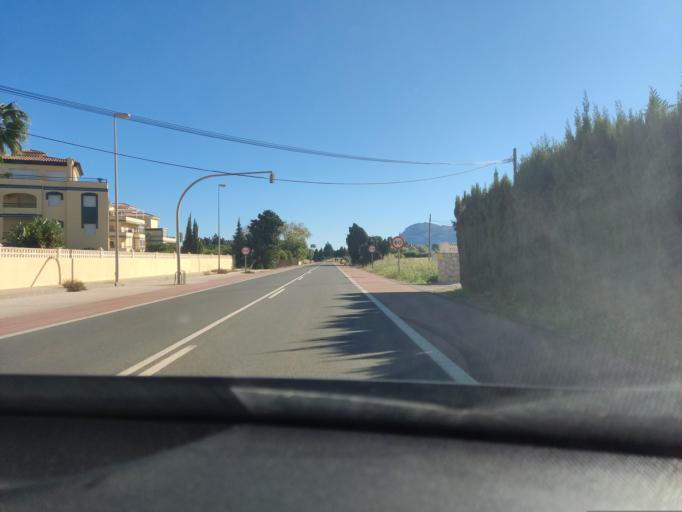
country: ES
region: Valencia
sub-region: Provincia de Alicante
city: els Poblets
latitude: 38.8590
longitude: 0.0321
